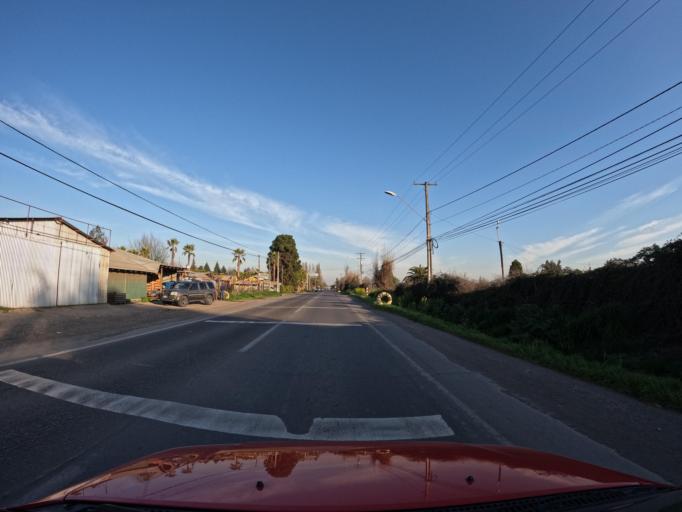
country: CL
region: Maule
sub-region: Provincia de Curico
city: Curico
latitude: -34.9496
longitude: -71.2576
